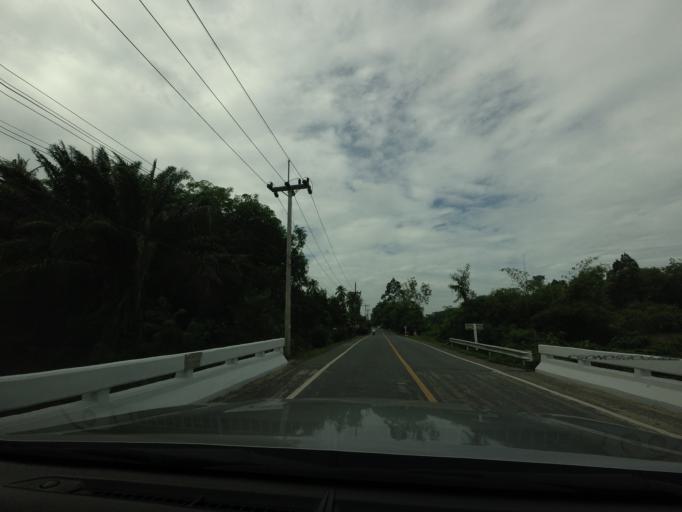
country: TH
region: Nakhon Si Thammarat
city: Phra Phrom
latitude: 8.2817
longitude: 99.9439
